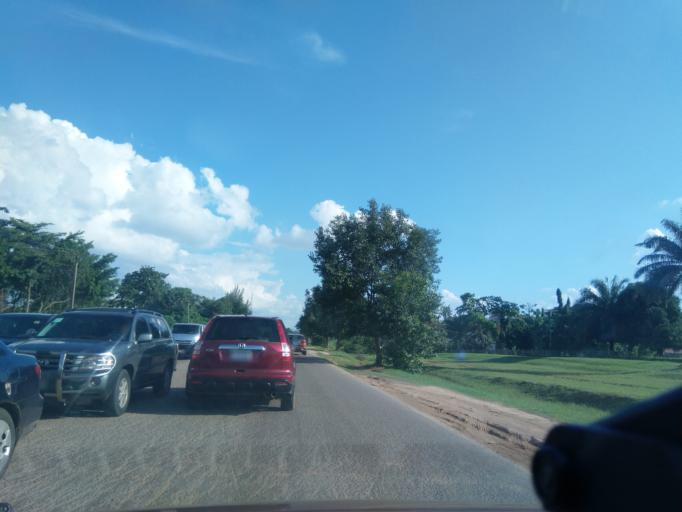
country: NG
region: Abuja Federal Capital Territory
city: Abuja
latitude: 9.0443
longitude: 7.4117
